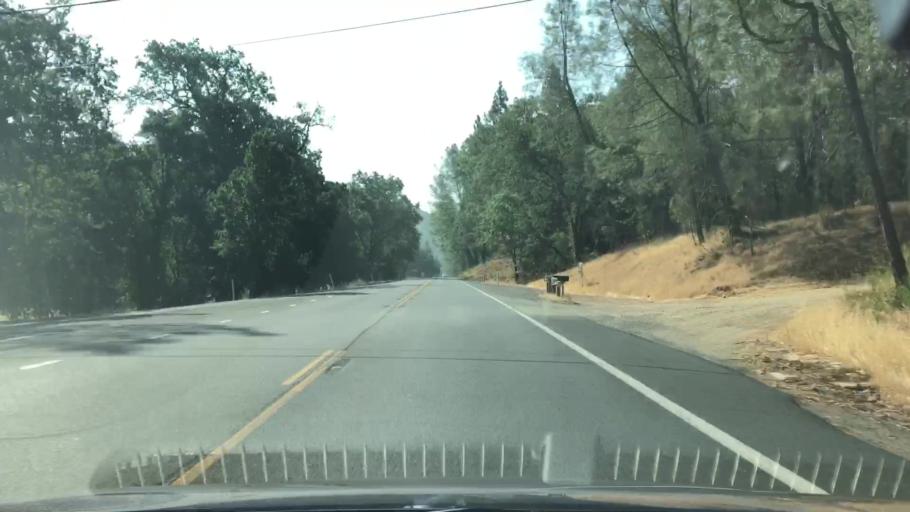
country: US
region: California
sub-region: Lake County
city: Middletown
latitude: 38.7037
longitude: -122.6050
